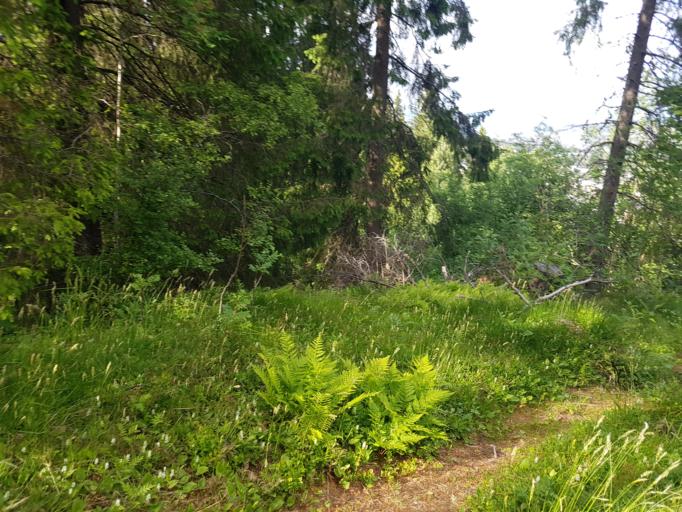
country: NO
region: Sor-Trondelag
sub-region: Trondheim
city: Trondheim
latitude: 63.4047
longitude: 10.3504
